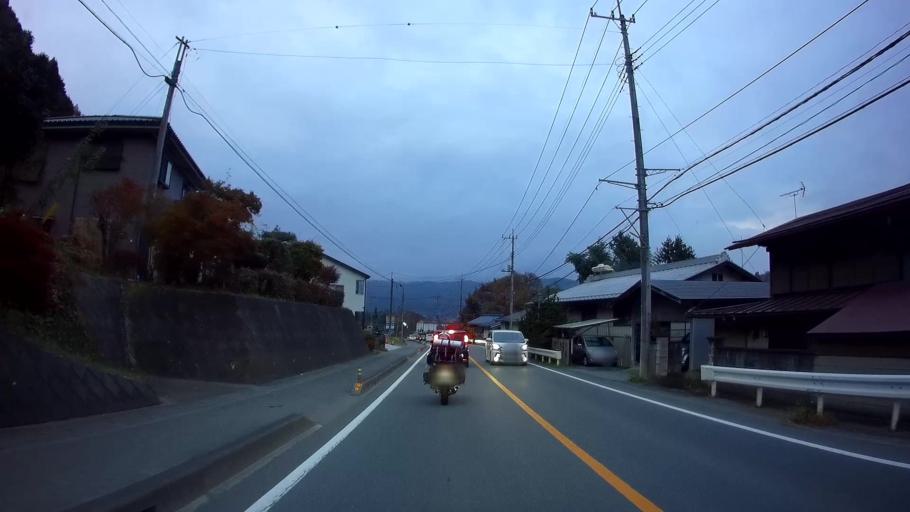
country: JP
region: Gunma
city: Nakanojomachi
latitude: 36.5543
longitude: 138.7785
